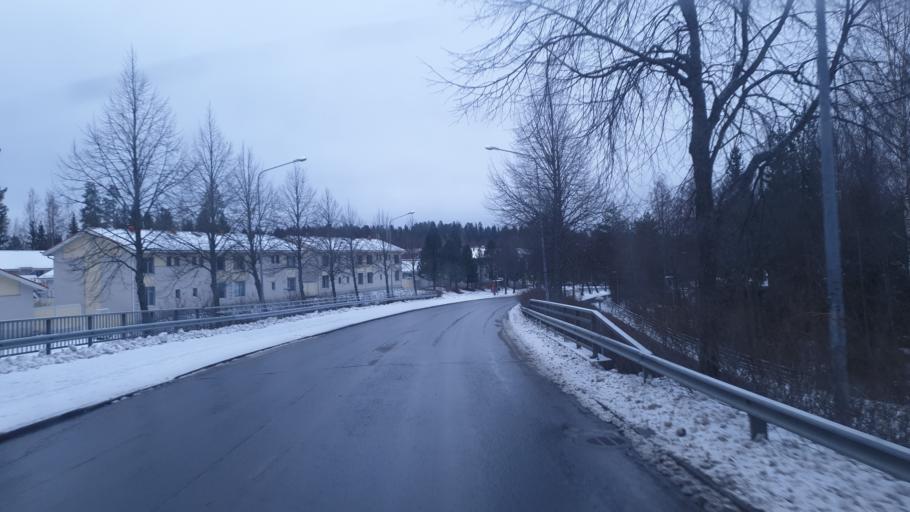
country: FI
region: Northern Savo
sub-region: Kuopio
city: Kuopio
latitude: 62.8377
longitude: 27.6350
